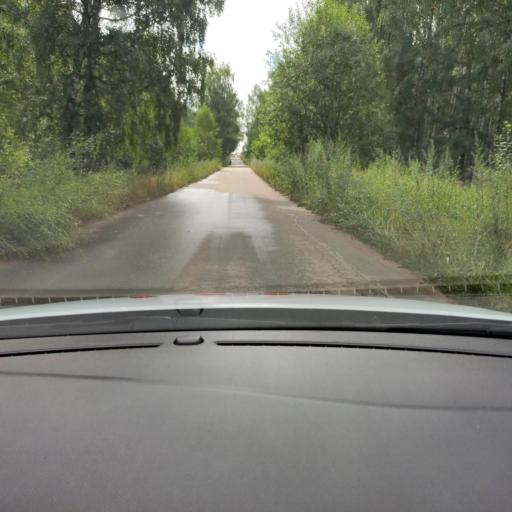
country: RU
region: Tatarstan
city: Staroye Arakchino
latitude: 55.8901
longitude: 49.0309
